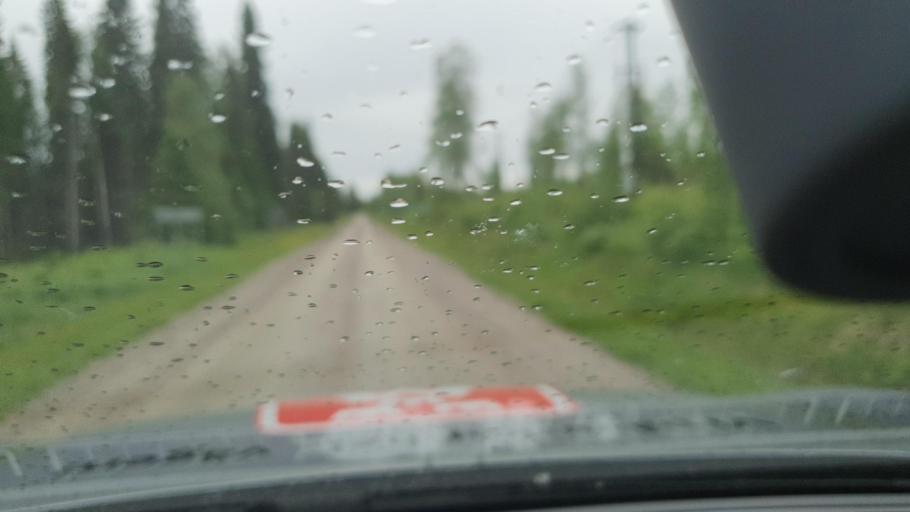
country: SE
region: Norrbotten
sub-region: Kalix Kommun
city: Rolfs
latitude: 66.0777
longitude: 22.9662
